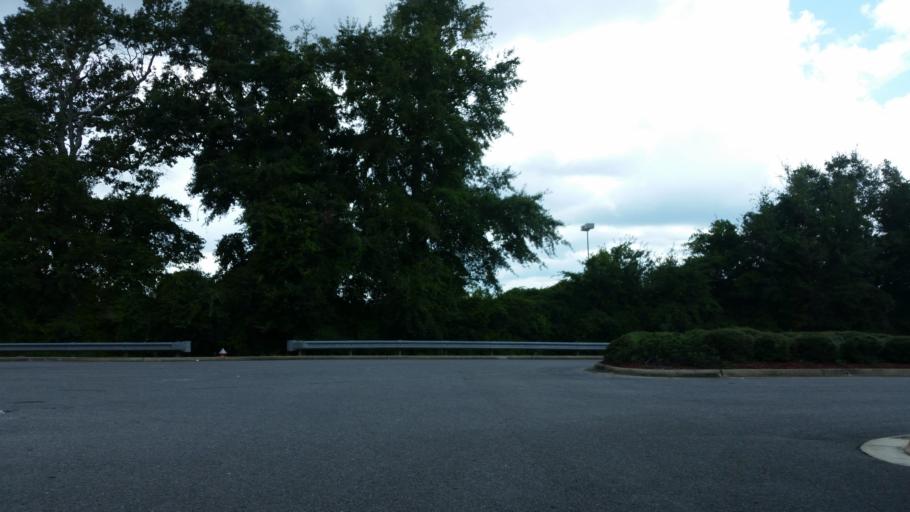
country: US
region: Florida
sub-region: Santa Rosa County
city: Pace
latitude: 30.6016
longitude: -87.1233
